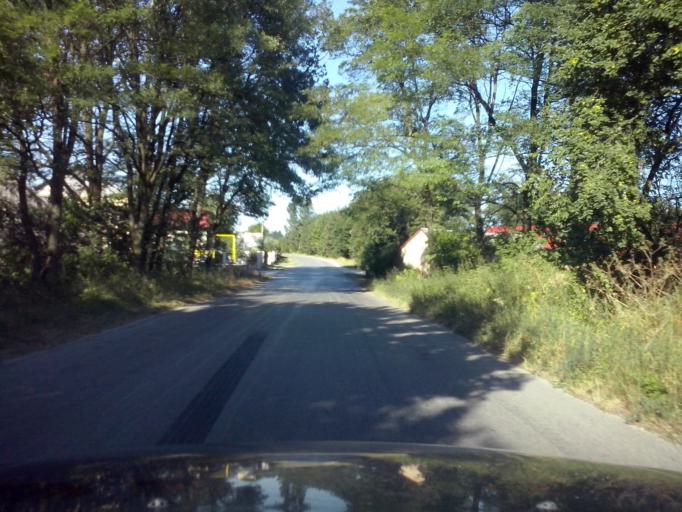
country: PL
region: Swietokrzyskie
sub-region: Powiat kielecki
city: Chmielnik
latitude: 50.5618
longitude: 20.6688
